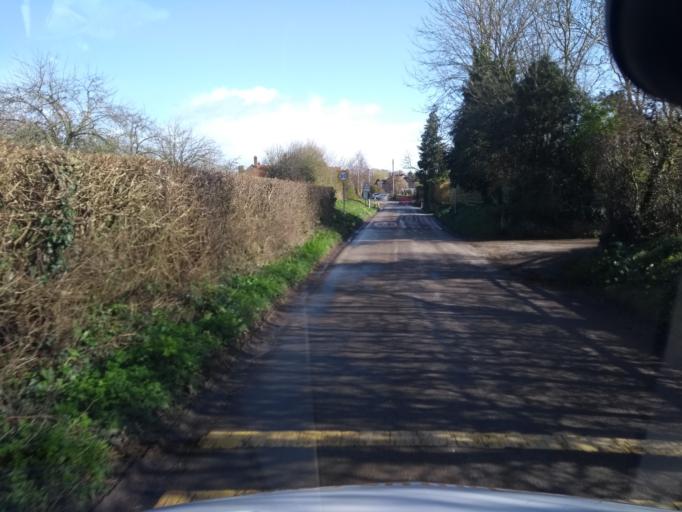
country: GB
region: England
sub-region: Somerset
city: South Petherton
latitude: 50.9753
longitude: -2.8228
